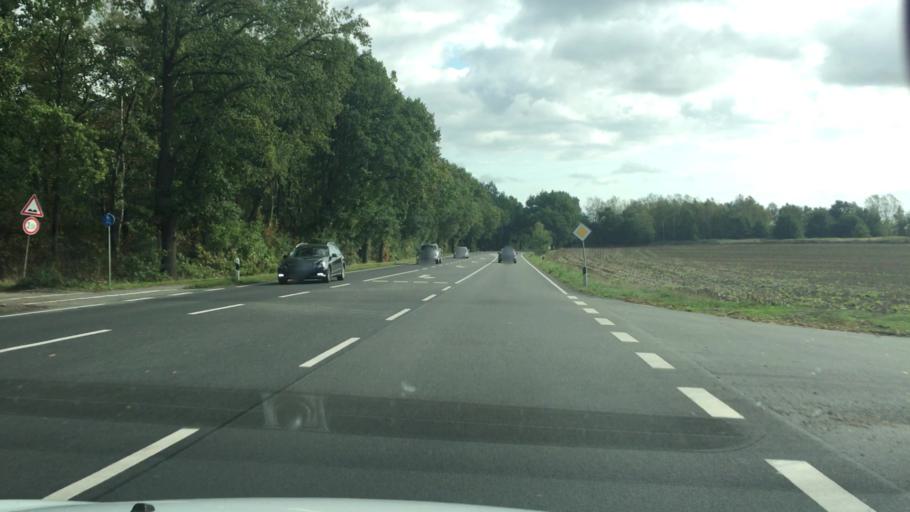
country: DE
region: Lower Saxony
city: Diepholz
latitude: 52.6457
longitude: 8.3418
